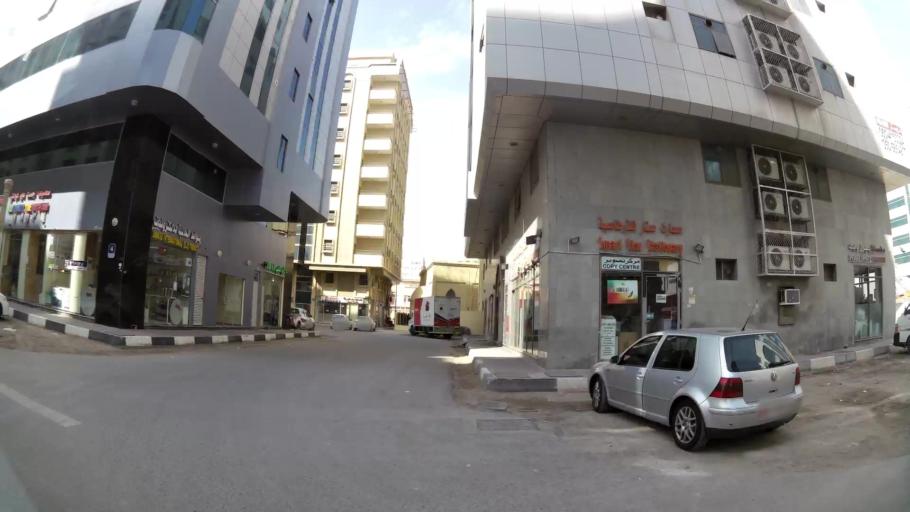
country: AE
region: Abu Dhabi
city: Abu Dhabi
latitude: 24.3410
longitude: 54.5335
